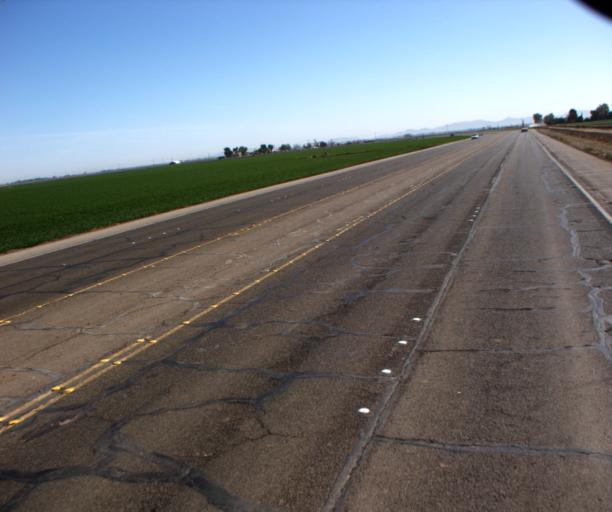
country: US
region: Arizona
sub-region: Yuma County
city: Somerton
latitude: 32.5673
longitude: -114.7781
